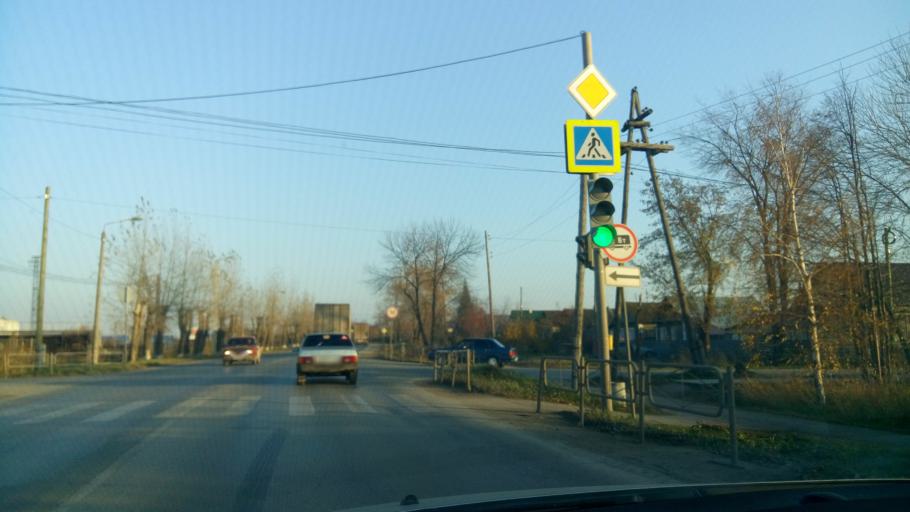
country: RU
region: Sverdlovsk
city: Bogdanovich
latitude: 56.7665
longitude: 62.0581
